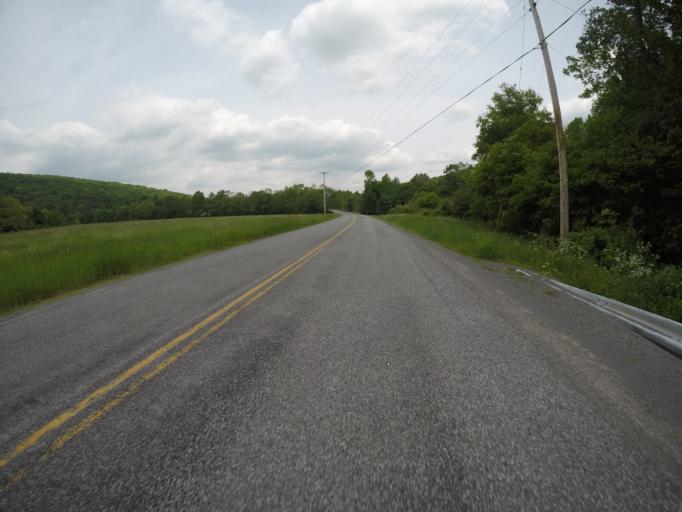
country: US
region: New York
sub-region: Delaware County
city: Stamford
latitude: 42.1567
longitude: -74.6848
